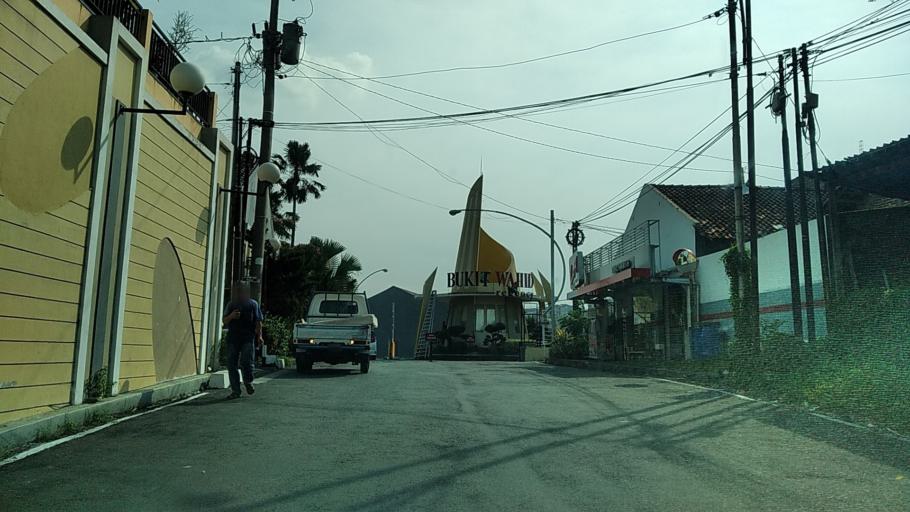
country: ID
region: Central Java
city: Semarang
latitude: -7.0021
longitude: 110.3875
